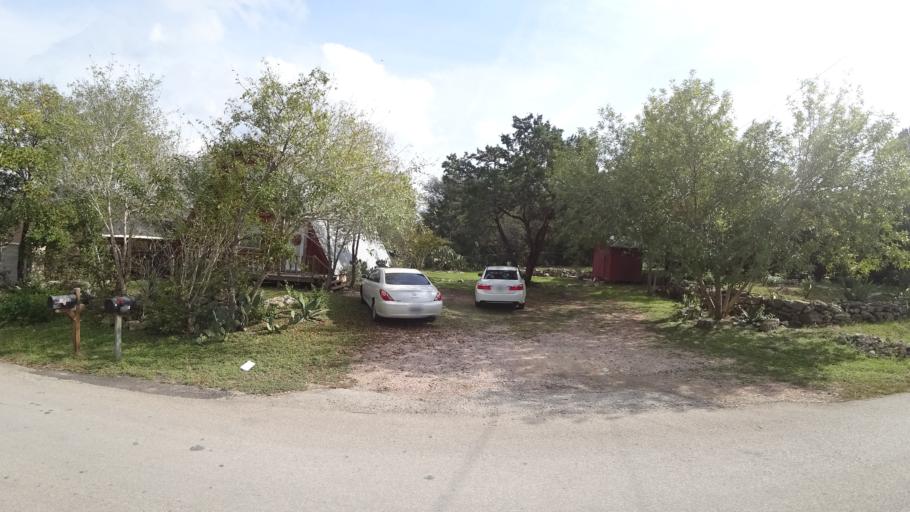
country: US
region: Texas
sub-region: Travis County
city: Hudson Bend
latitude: 30.3767
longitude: -97.9337
